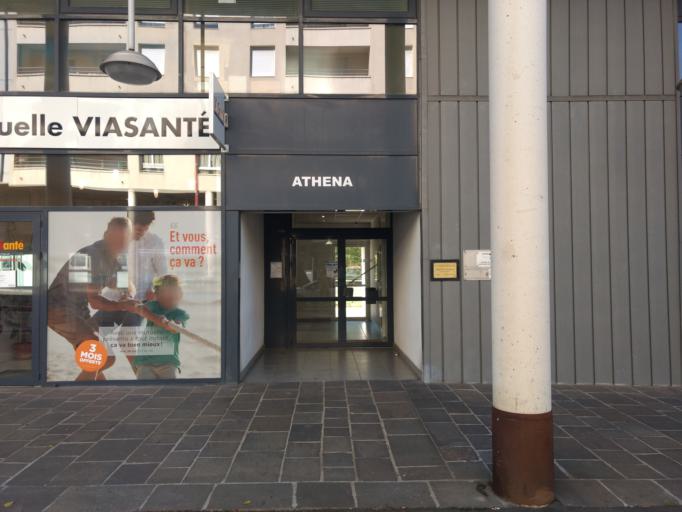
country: FR
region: Midi-Pyrenees
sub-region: Departement de l'Aveyron
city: Olemps
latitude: 44.3586
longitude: 2.5570
